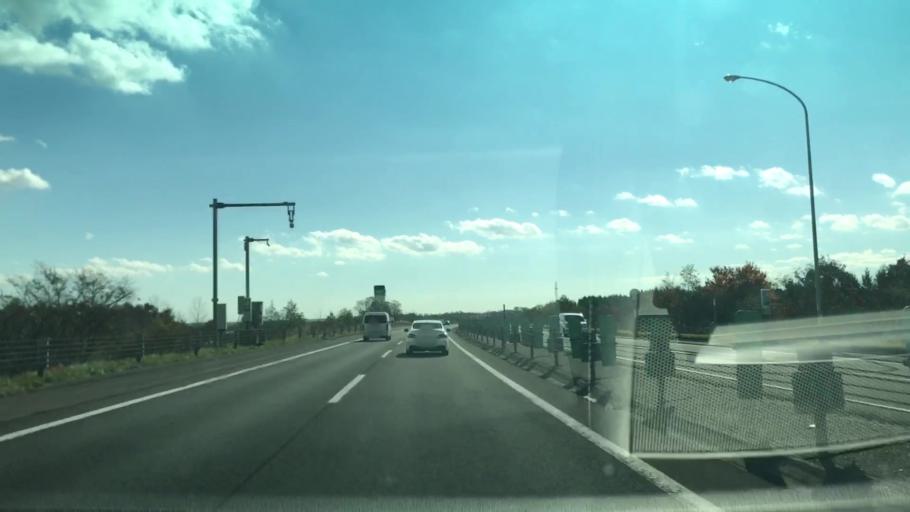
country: JP
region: Hokkaido
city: Kitahiroshima
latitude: 42.9083
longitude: 141.5503
